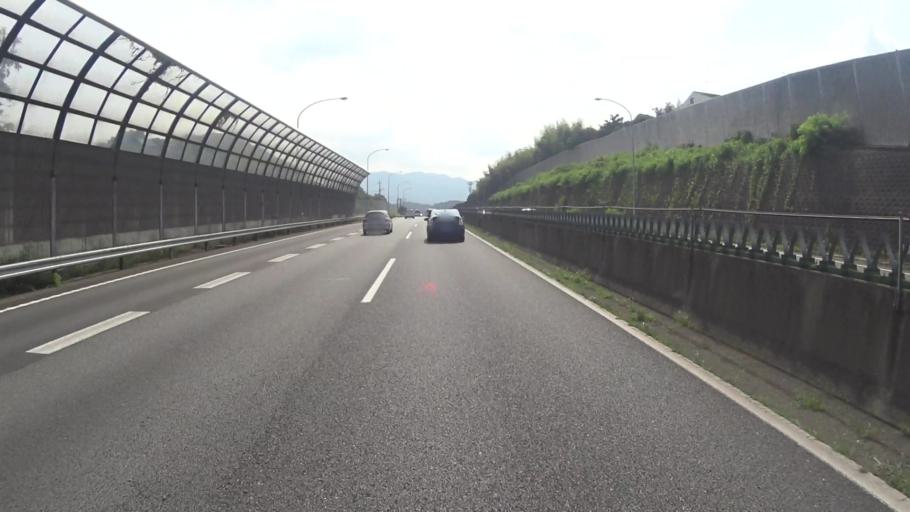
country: JP
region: Kyoto
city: Uji
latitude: 34.9567
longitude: 135.7858
